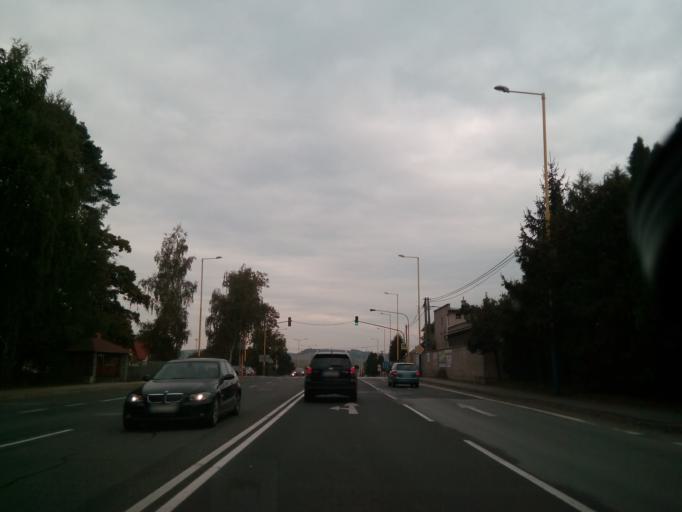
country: SK
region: Presovsky
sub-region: Okres Presov
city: Presov
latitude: 49.0423
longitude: 21.3313
